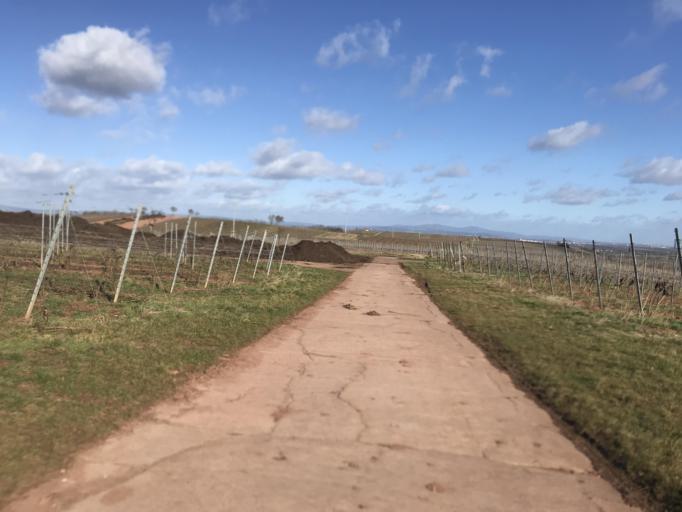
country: DE
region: Rheinland-Pfalz
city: Nackenheim
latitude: 49.8950
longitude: 8.3348
